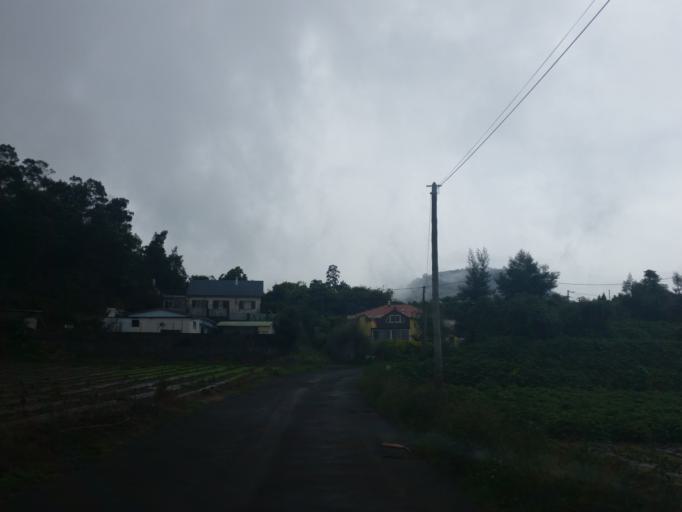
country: RE
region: Reunion
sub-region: Reunion
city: Le Tampon
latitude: -21.2279
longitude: 55.5275
